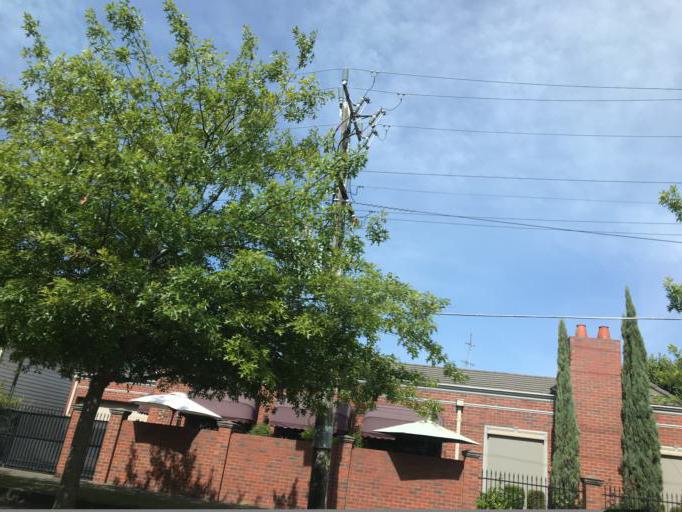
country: AU
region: Victoria
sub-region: Ballarat North
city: Ballarat
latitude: -37.5624
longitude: 143.8425
